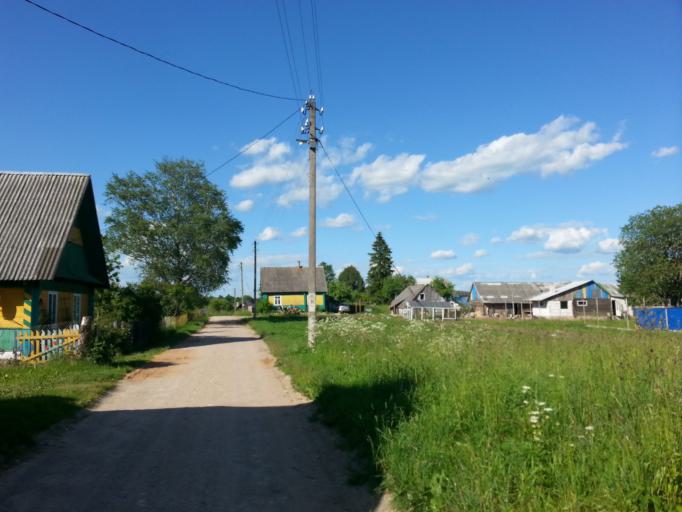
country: BY
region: Minsk
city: Narach
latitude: 54.9774
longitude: 26.6145
